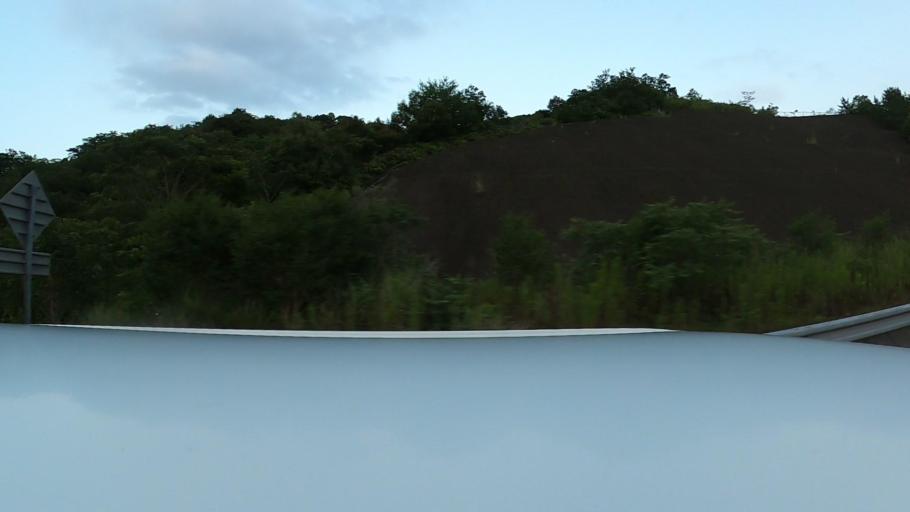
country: JP
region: Miyazaki
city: Nobeoka
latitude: 32.4581
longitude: 131.6147
